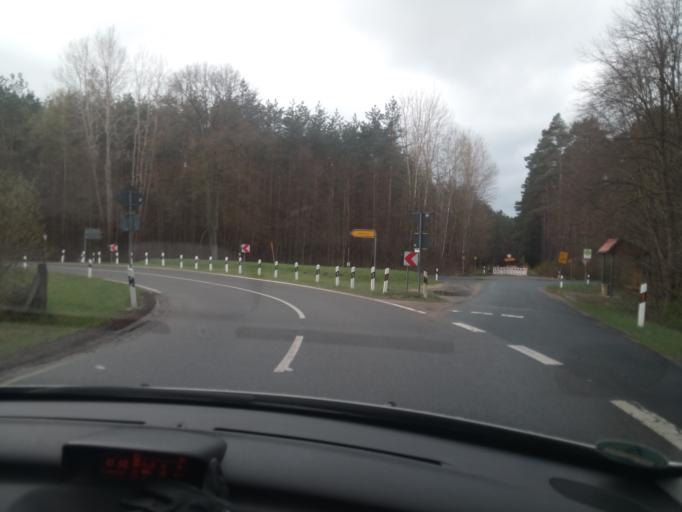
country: DE
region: Mecklenburg-Vorpommern
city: Carpin
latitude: 53.3221
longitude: 13.3384
